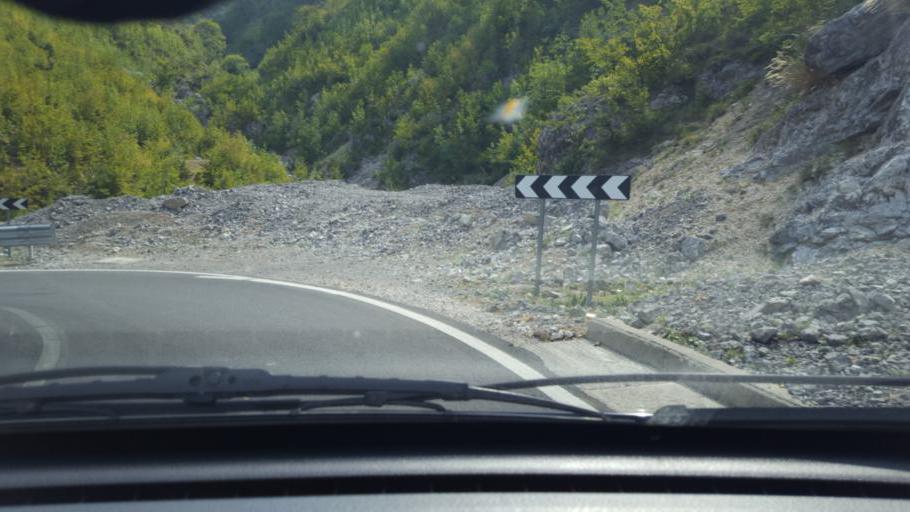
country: AL
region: Shkoder
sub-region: Rrethi i Malesia e Madhe
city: Kastrat
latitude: 42.4125
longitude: 19.5099
